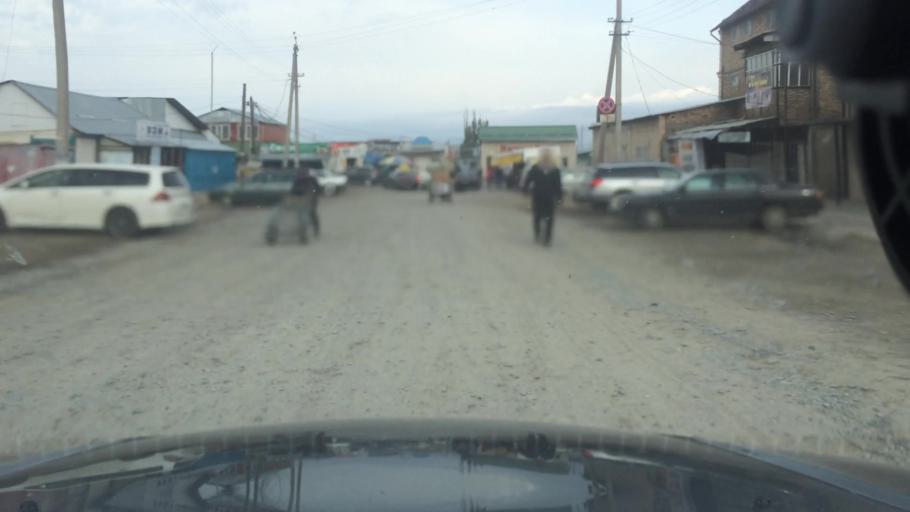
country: KG
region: Ysyk-Koel
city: Karakol
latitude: 42.4917
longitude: 78.3861
